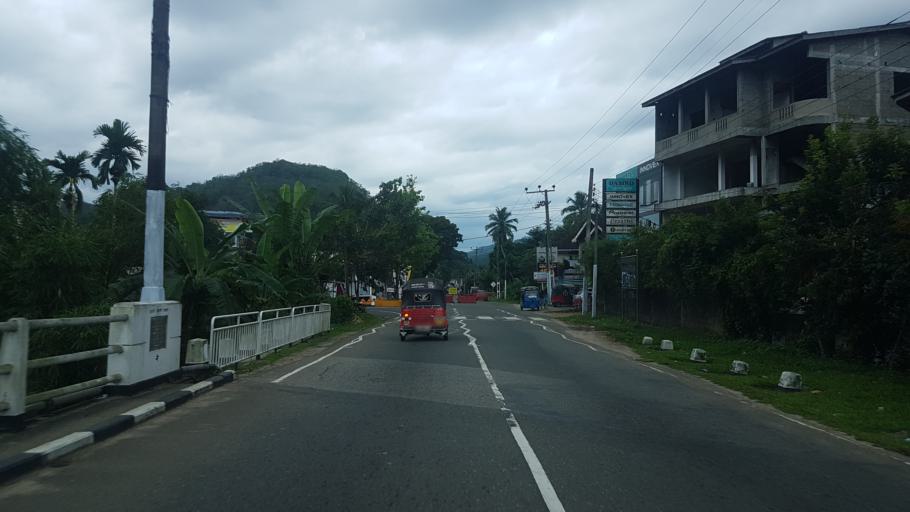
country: LK
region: Western
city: Hanwella Ihala
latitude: 7.0325
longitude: 80.2940
